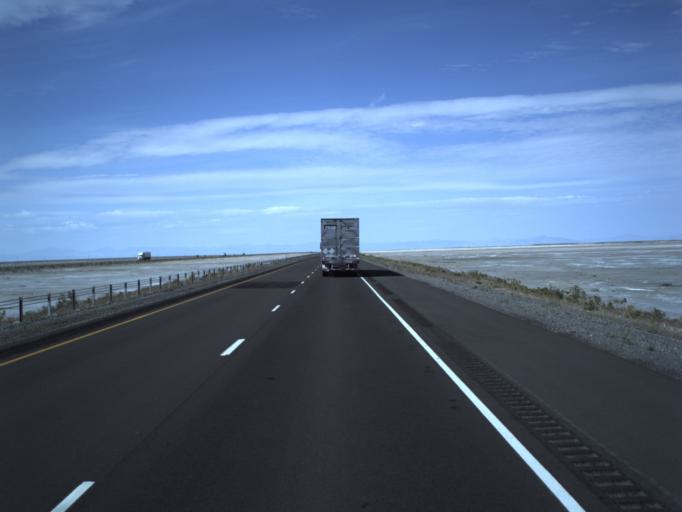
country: US
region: Utah
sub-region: Tooele County
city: Wendover
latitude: 40.7284
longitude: -113.3265
